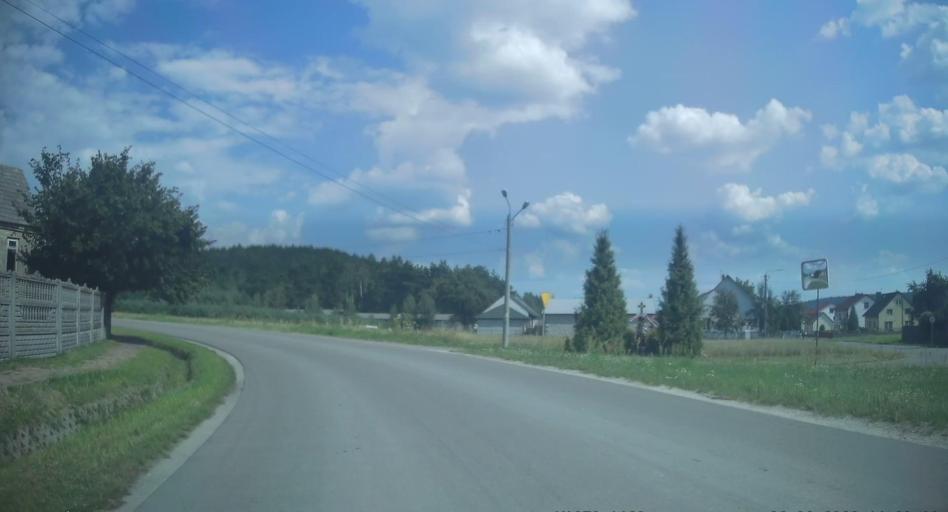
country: PL
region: Swietokrzyskie
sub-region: Powiat kielecki
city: Checiny
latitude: 50.8145
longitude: 20.4064
